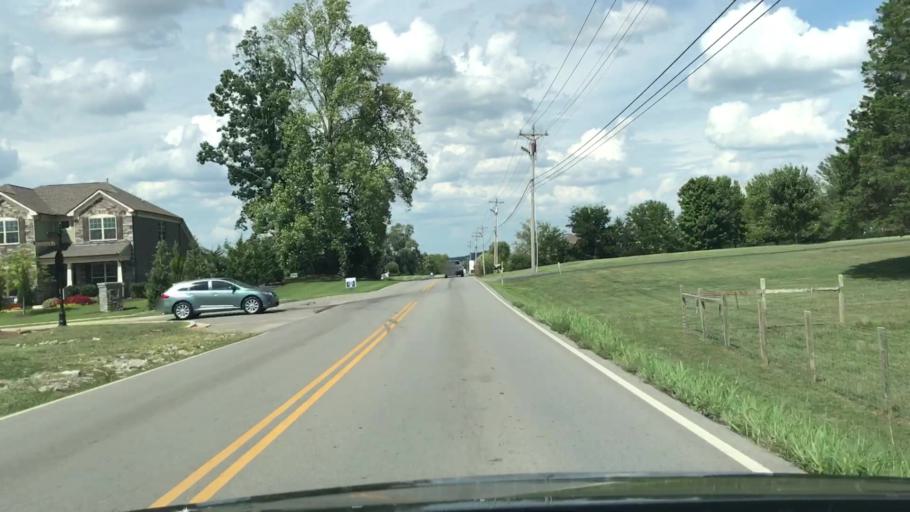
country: US
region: Tennessee
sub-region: Maury County
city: Spring Hill
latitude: 35.7570
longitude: -86.8830
